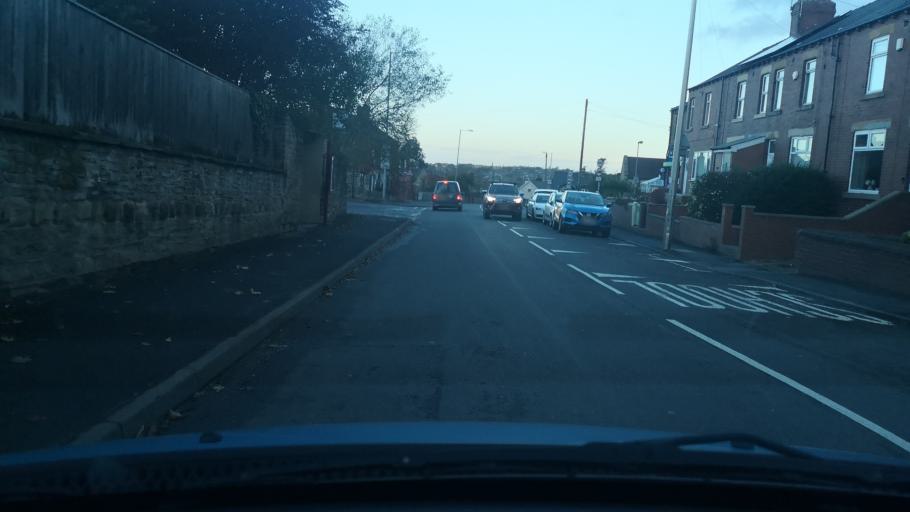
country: GB
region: England
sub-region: City and Borough of Wakefield
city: Horbury
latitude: 53.6486
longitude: -1.5754
